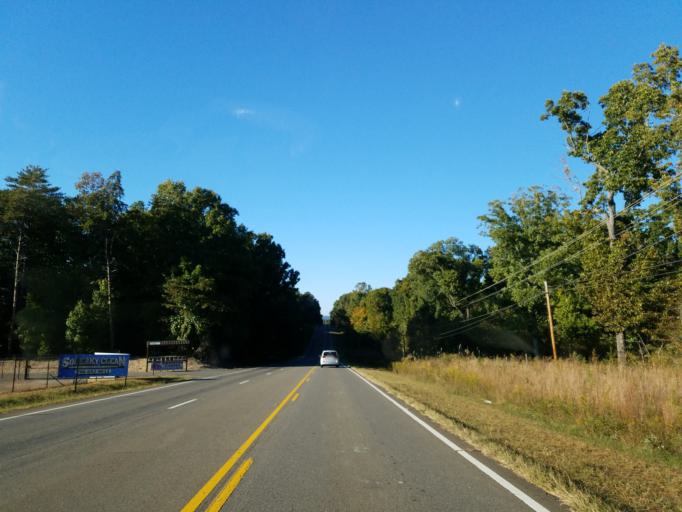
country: US
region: Georgia
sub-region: Pickens County
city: Nelson
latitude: 34.4011
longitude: -84.3837
